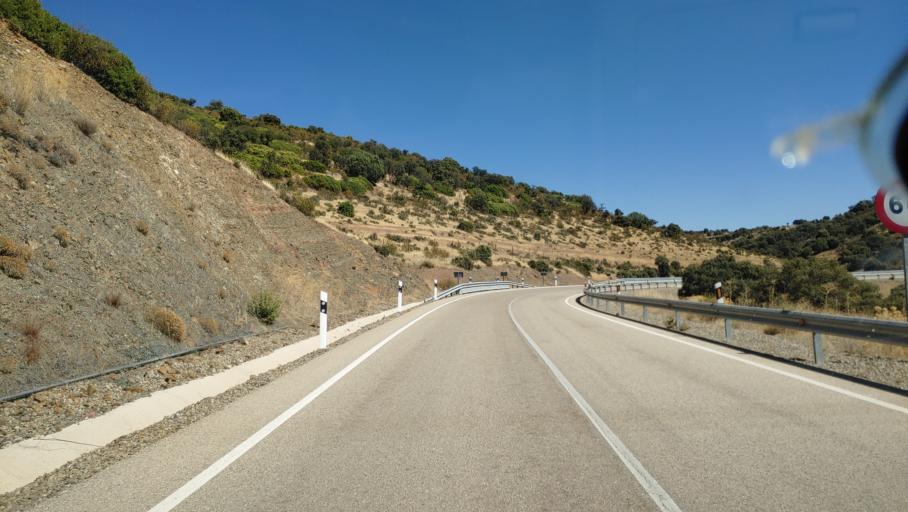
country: ES
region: Andalusia
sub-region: Provincia de Jaen
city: Genave
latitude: 38.4987
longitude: -2.7679
